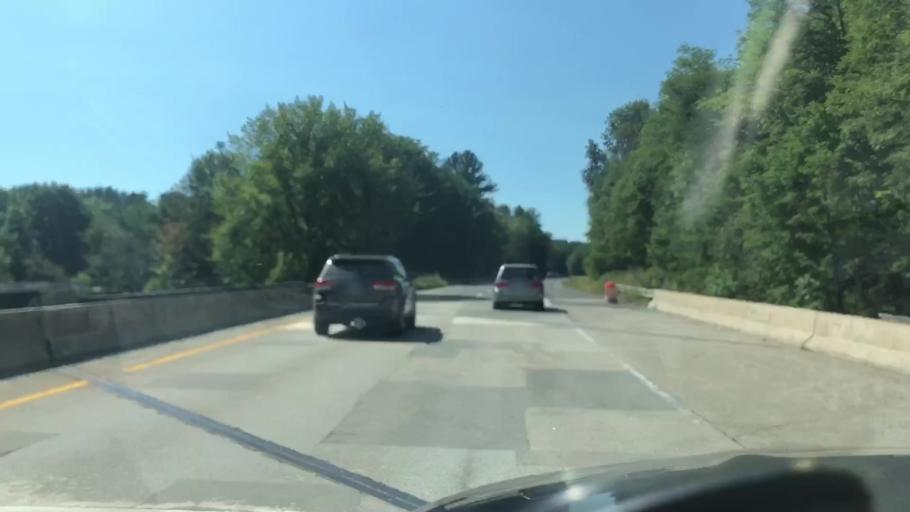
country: US
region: Massachusetts
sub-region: Franklin County
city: Bernardston
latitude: 42.6618
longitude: -72.5462
